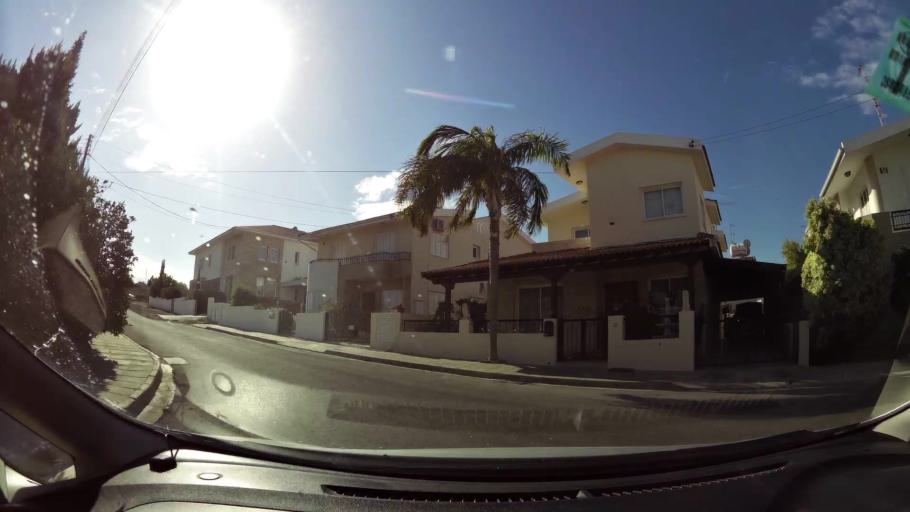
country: CY
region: Lefkosia
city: Nicosia
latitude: 35.1263
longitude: 33.3420
